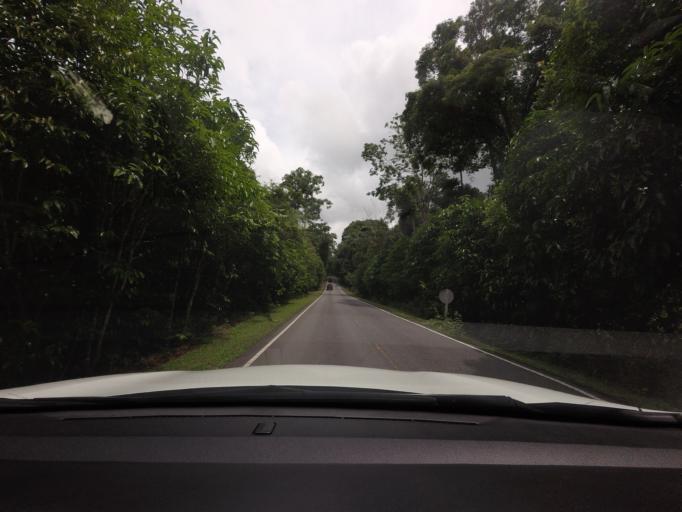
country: TH
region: Nakhon Ratchasima
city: Pak Chong
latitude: 14.4444
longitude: 101.3687
